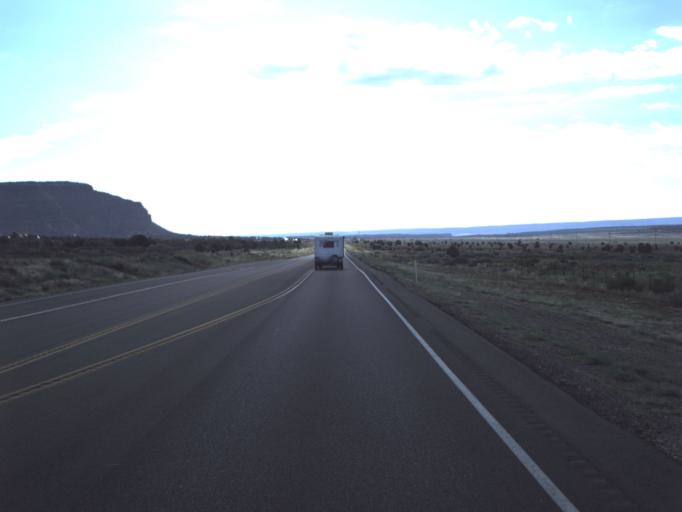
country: US
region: Utah
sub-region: Kane County
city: Kanab
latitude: 37.0287
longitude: -112.4834
